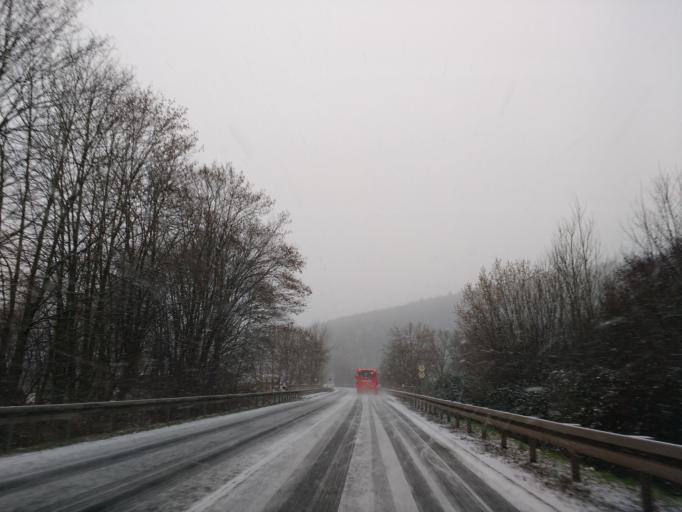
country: DE
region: Hesse
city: Melsungen
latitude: 51.1105
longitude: 9.5604
